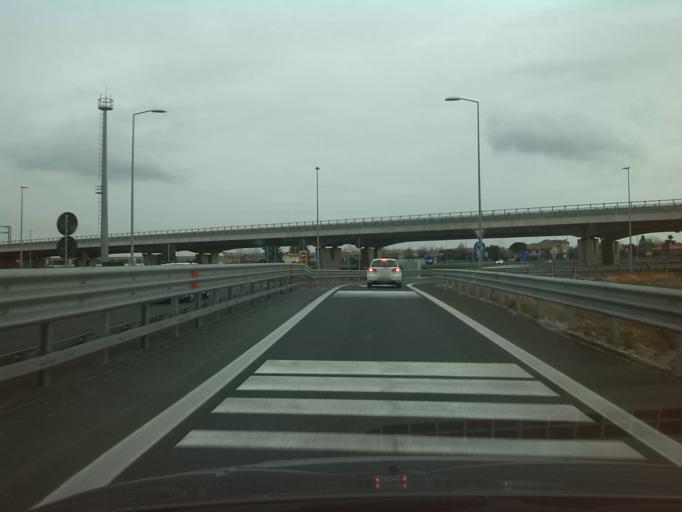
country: IT
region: Friuli Venezia Giulia
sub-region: Provincia di Gorizia
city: Villesse
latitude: 45.8698
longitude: 13.4421
